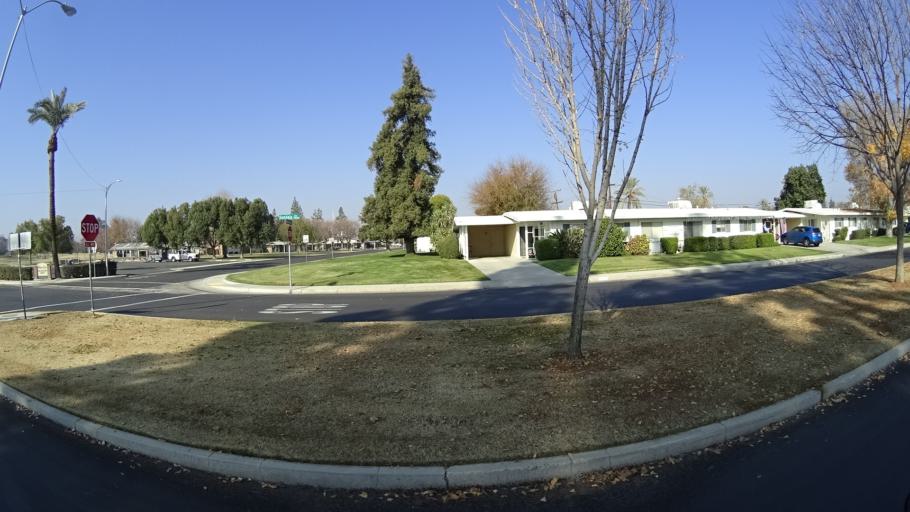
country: US
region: California
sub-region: Kern County
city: Bakersfield
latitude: 35.3438
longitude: -119.0661
